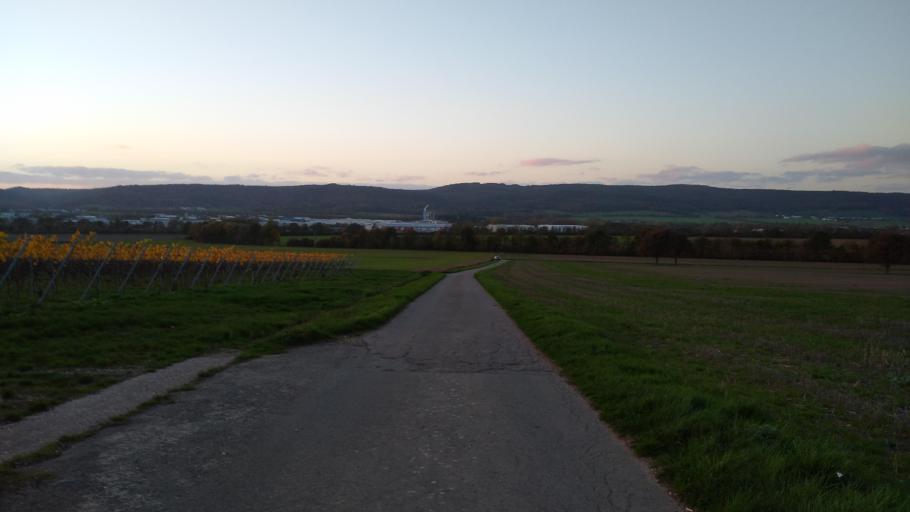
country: DE
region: Rheinland-Pfalz
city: Bekond
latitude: 49.8564
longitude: 6.8176
